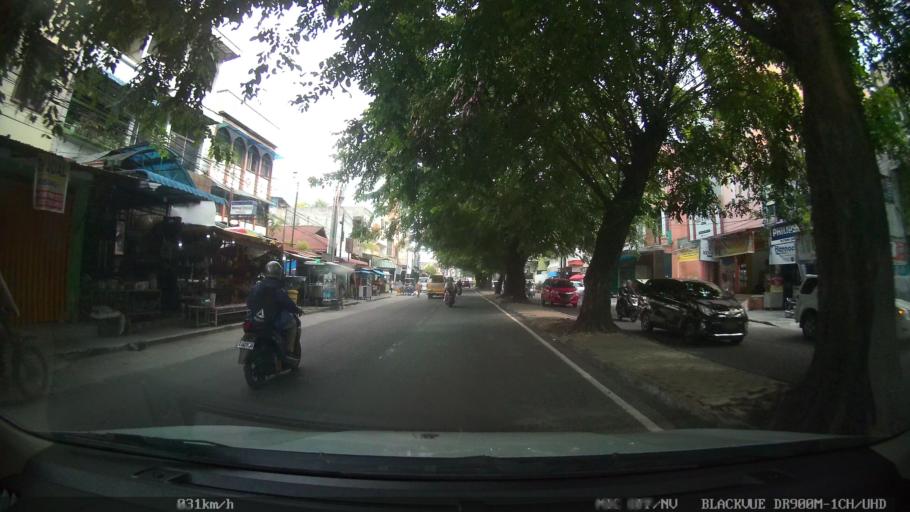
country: ID
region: North Sumatra
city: Medan
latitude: 3.5548
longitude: 98.6884
